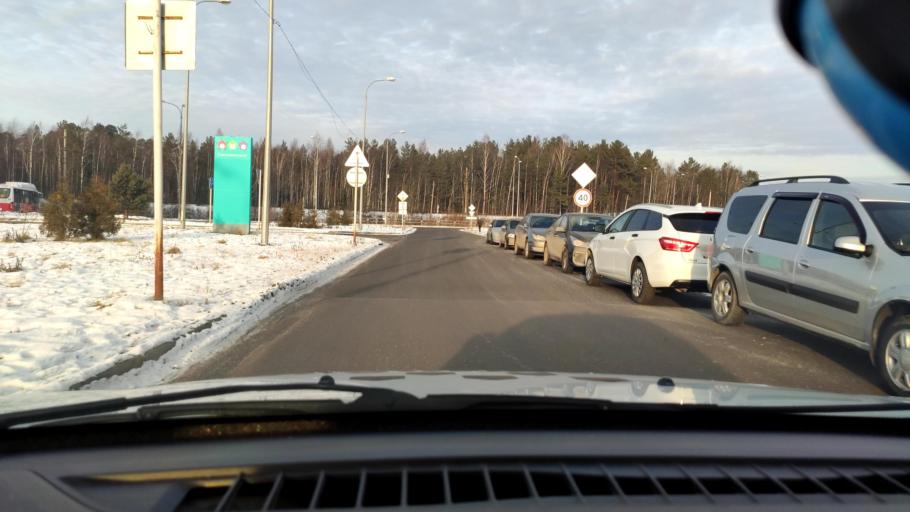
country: RU
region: Perm
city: Perm
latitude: 58.0341
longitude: 56.1776
